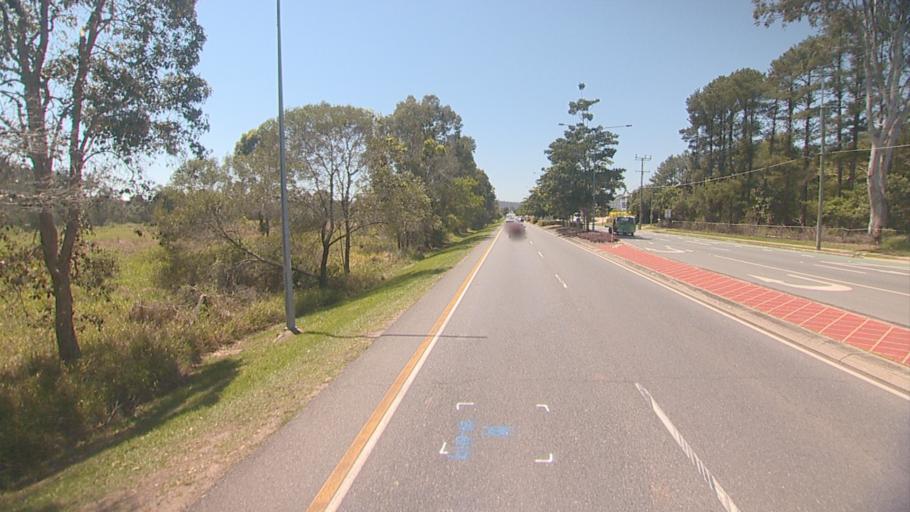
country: AU
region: Queensland
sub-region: Logan
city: Woodridge
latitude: -27.6181
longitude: 153.1014
